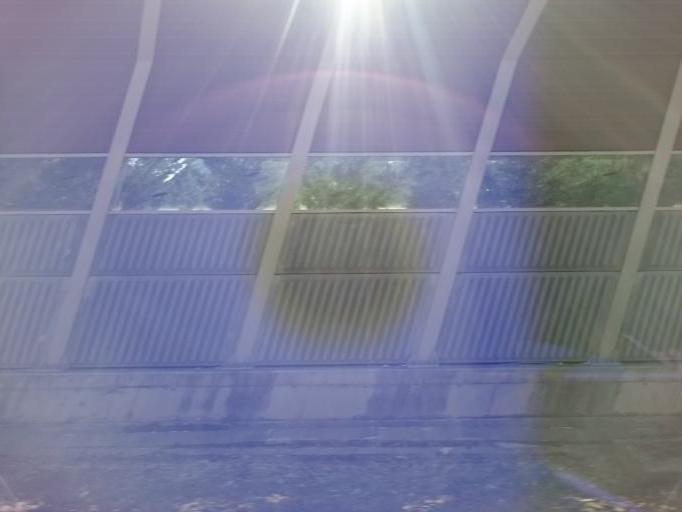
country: IT
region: Trentino-Alto Adige
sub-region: Provincia di Trento
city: Mattarello
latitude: 46.0014
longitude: 11.1240
